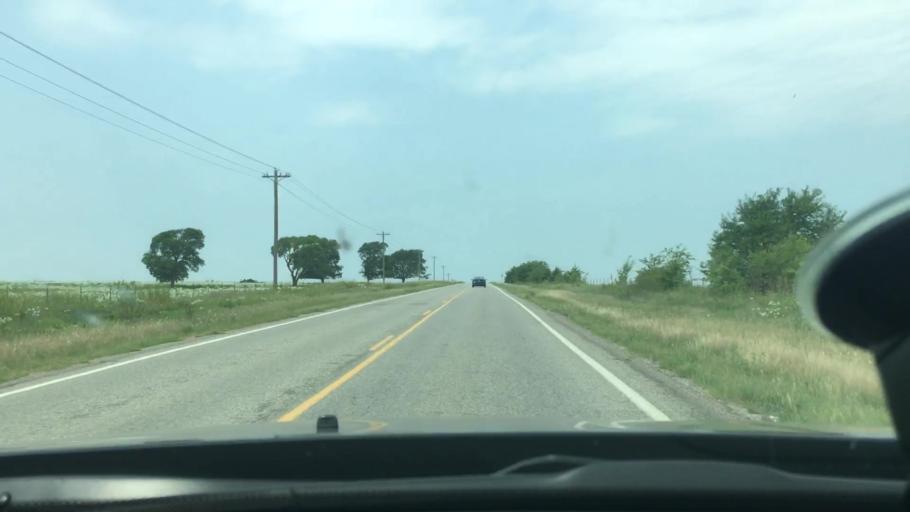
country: US
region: Oklahoma
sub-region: Marshall County
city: Kingston
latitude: 33.9983
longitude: -96.7871
